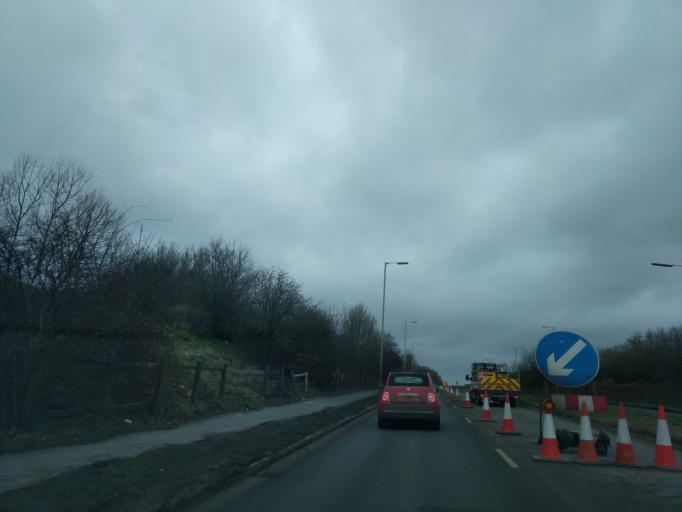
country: GB
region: England
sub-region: Staffordshire
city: Cannock
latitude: 52.6827
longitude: -2.0166
